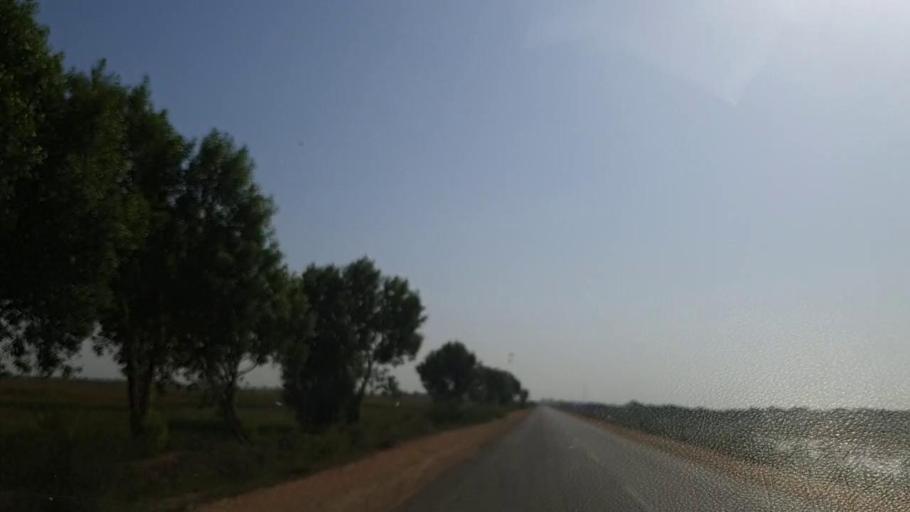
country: PK
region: Sindh
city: Jati
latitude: 24.5332
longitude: 68.2784
